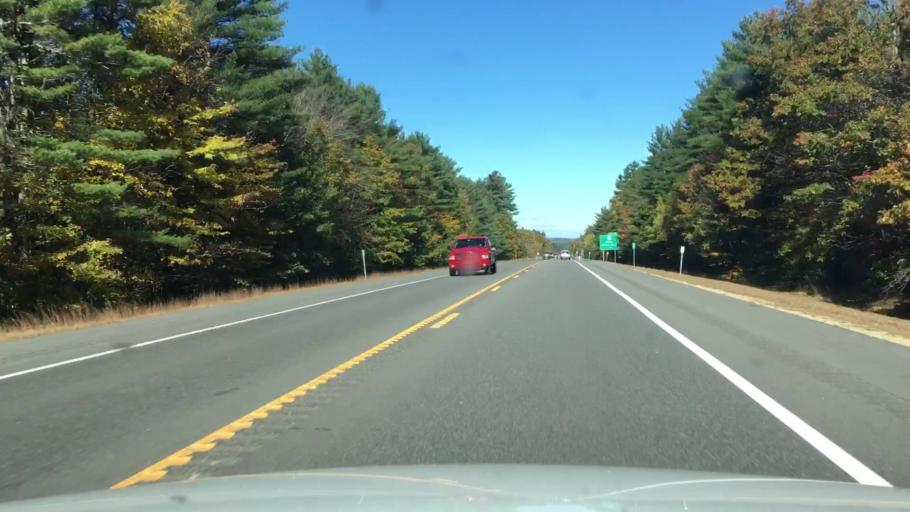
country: US
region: New Hampshire
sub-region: Strafford County
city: Farmington
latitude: 43.4611
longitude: -70.9955
